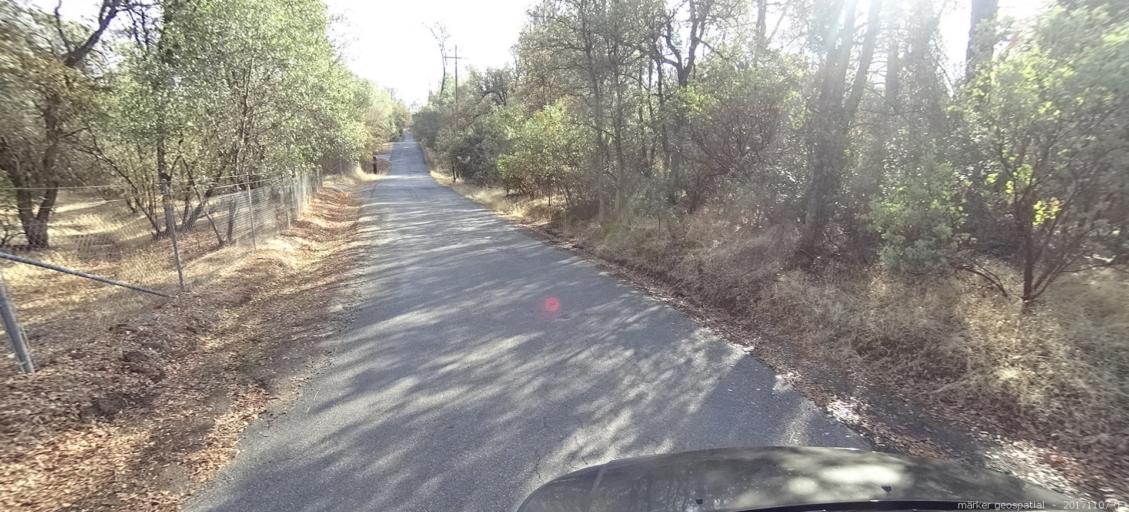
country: US
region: California
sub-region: Shasta County
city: Shasta
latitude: 40.5356
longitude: -122.4557
